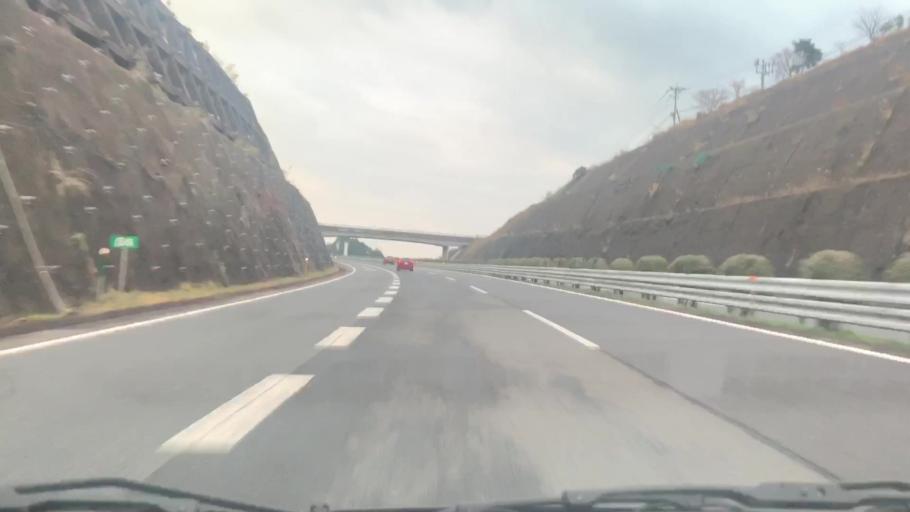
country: JP
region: Nagasaki
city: Omura
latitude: 32.9979
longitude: 129.9510
